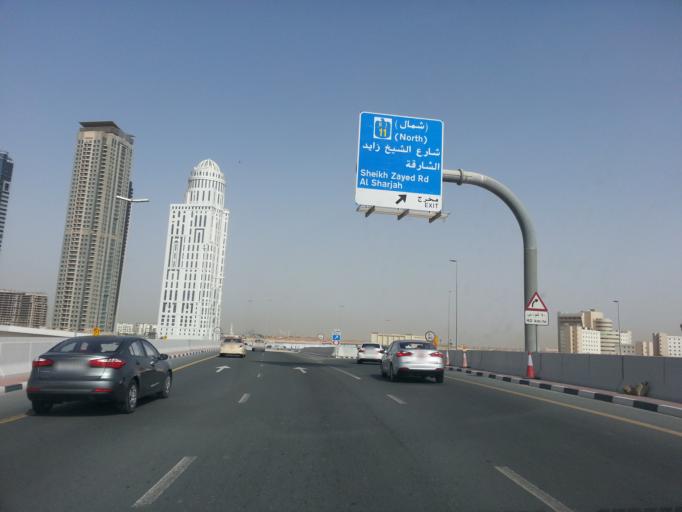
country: AE
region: Dubai
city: Dubai
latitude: 25.0636
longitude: 55.1326
